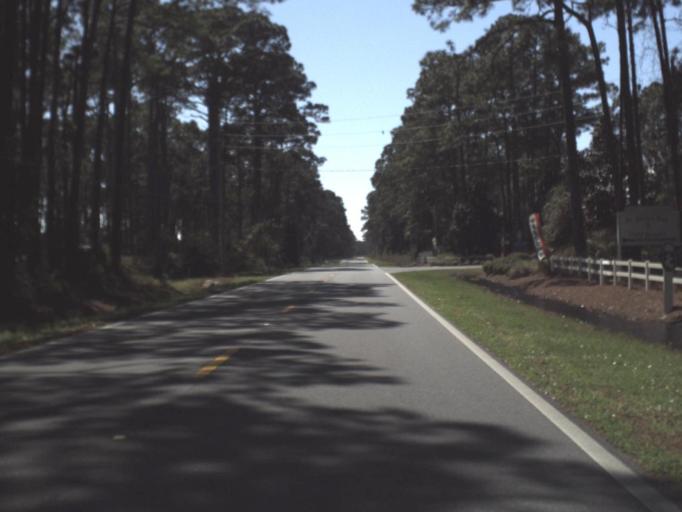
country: US
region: Florida
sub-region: Franklin County
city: Carrabelle
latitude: 29.8962
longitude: -84.5612
